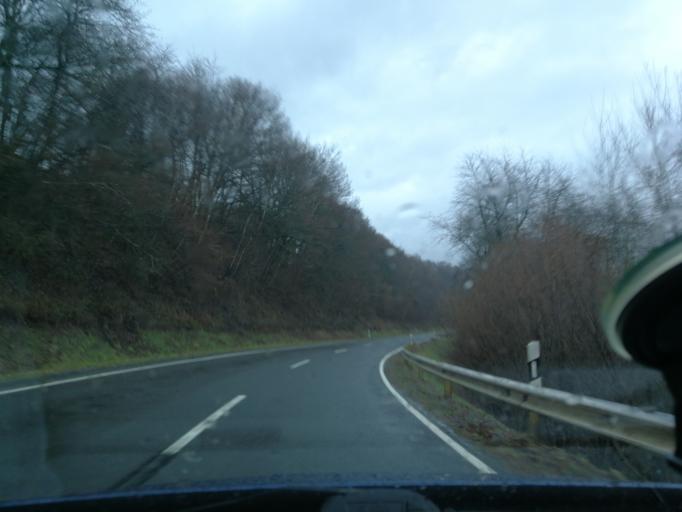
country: DE
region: Rheinland-Pfalz
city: Deuselbach
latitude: 49.7566
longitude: 7.0501
